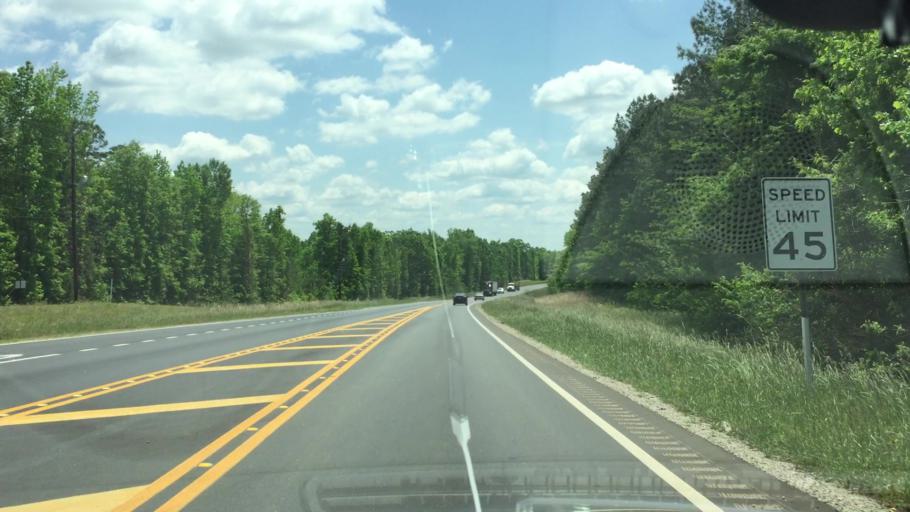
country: US
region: Alabama
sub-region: Lee County
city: Opelika
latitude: 32.6636
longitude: -85.3640
